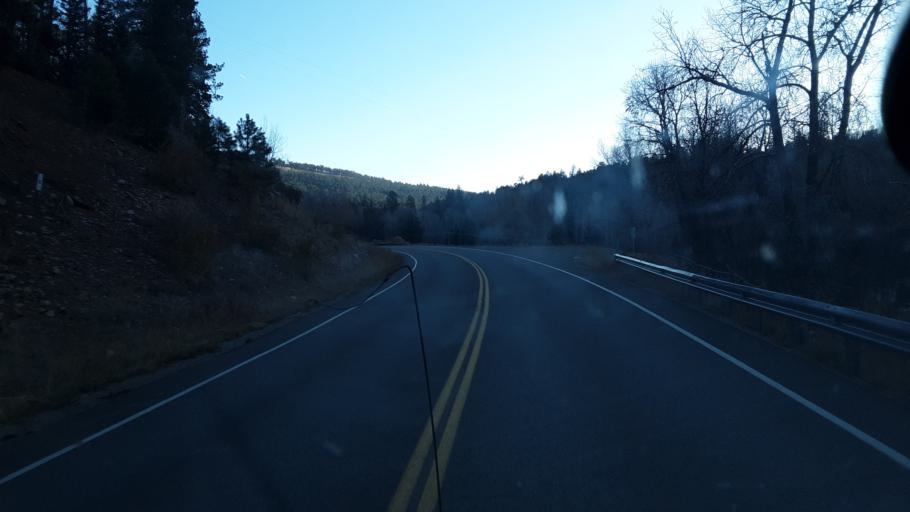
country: US
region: Colorado
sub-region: La Plata County
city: Bayfield
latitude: 37.3540
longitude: -107.6824
